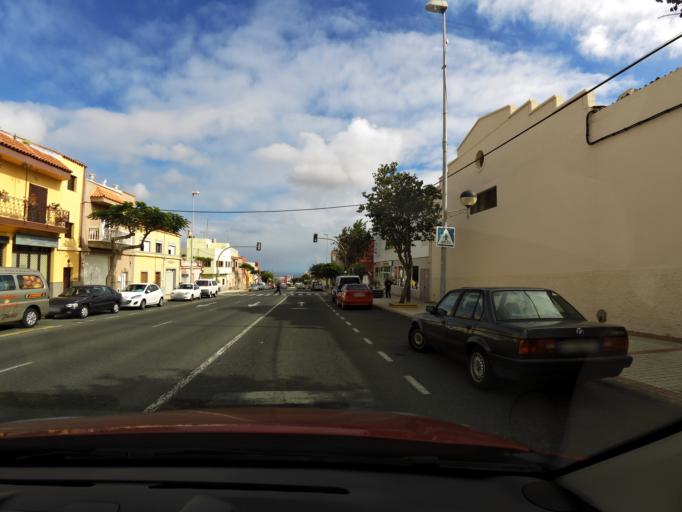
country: ES
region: Canary Islands
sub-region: Provincia de Las Palmas
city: Ingenio
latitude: 27.9181
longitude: -15.4321
